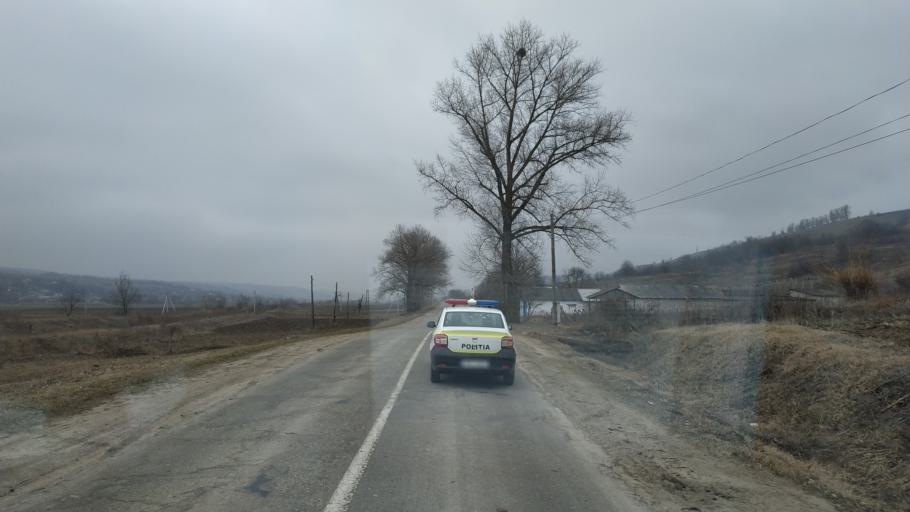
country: MD
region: Hincesti
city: Hincesti
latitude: 46.9740
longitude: 28.4718
